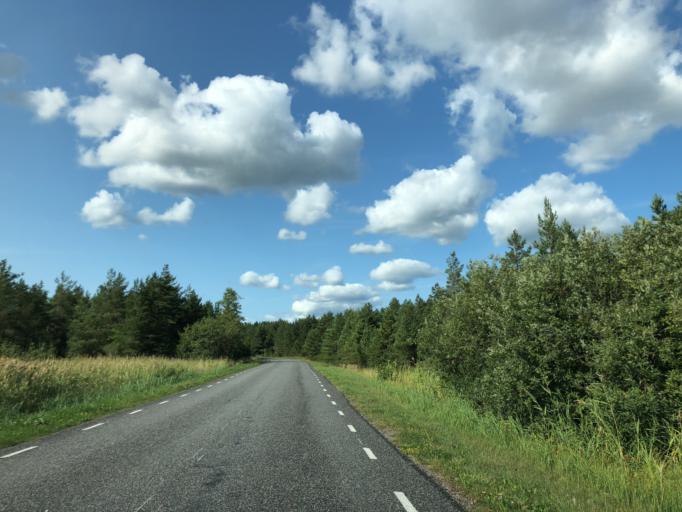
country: EE
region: Hiiumaa
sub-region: Kaerdla linn
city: Kardla
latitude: 58.8044
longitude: 22.7453
